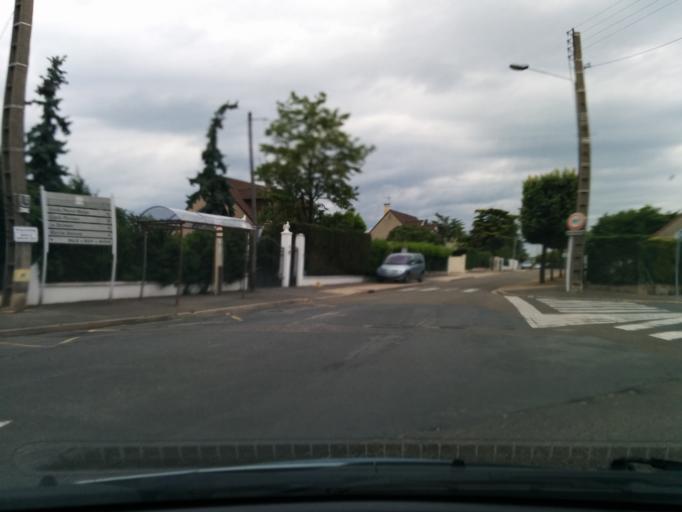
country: FR
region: Ile-de-France
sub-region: Departement des Yvelines
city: Epone
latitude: 48.9682
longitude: 1.8297
